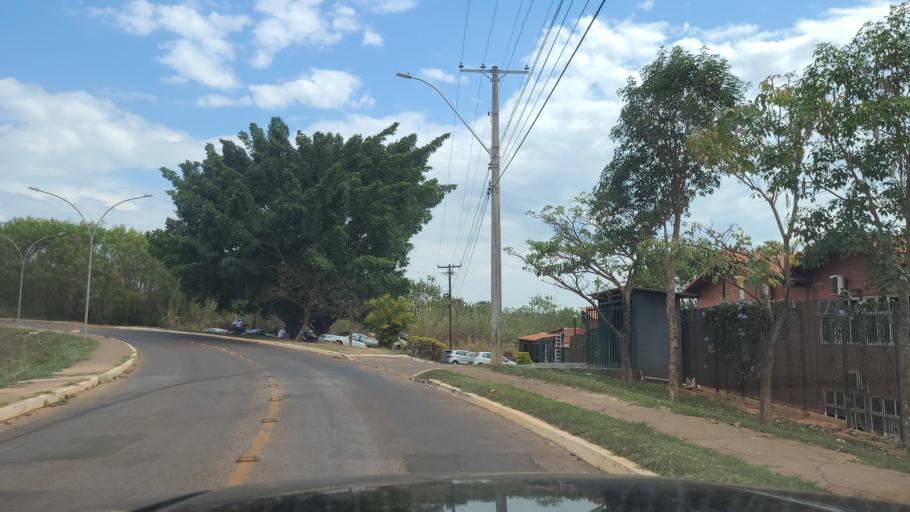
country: BR
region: Federal District
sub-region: Brasilia
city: Brasilia
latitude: -15.8544
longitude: -47.8504
